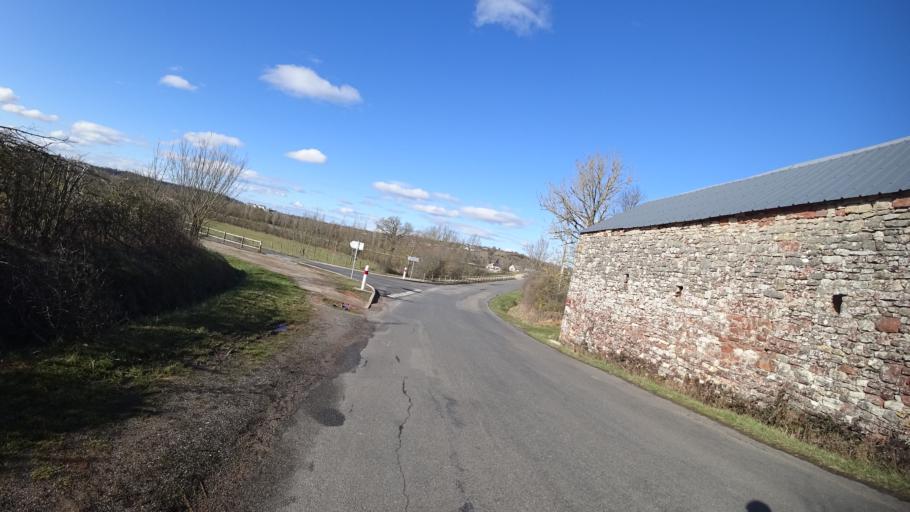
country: FR
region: Midi-Pyrenees
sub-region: Departement de l'Aveyron
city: Sebazac-Concoures
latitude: 44.3735
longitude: 2.6079
